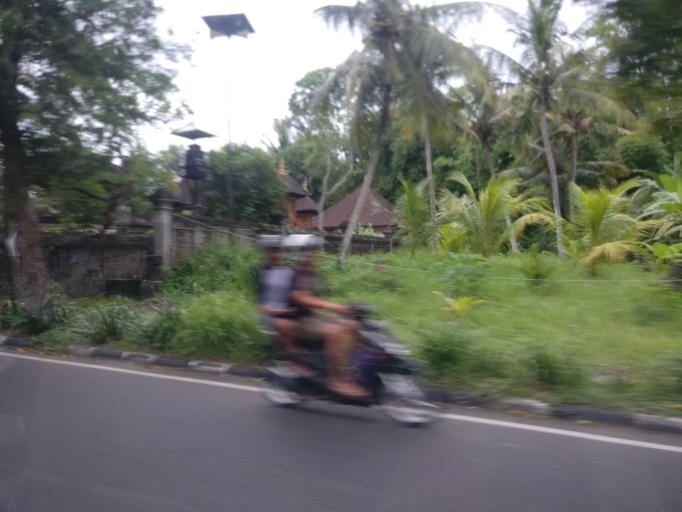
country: ID
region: Bali
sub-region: Kabupaten Gianyar
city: Ubud
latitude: -8.5566
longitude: 115.3022
